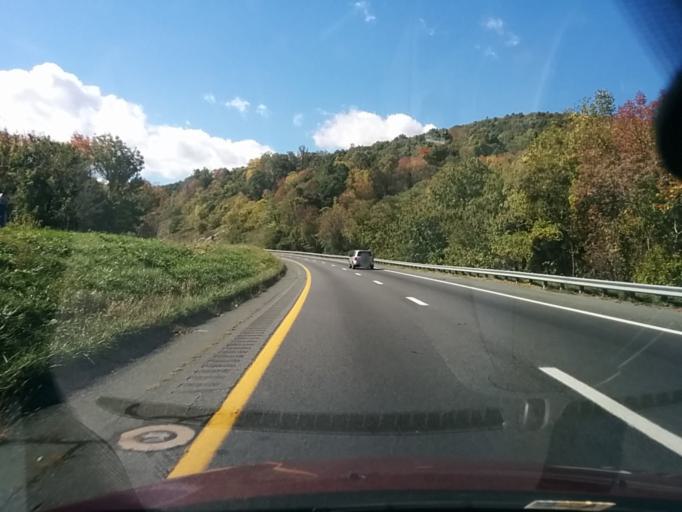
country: US
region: Virginia
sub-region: Augusta County
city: Dooms
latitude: 38.0443
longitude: -78.8149
